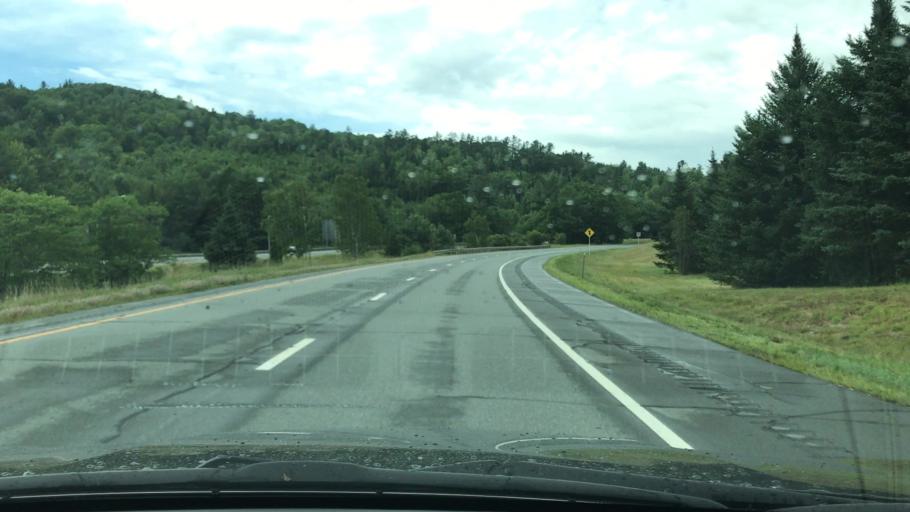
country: US
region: New Hampshire
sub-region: Grafton County
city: Littleton
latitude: 44.3090
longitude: -71.7989
